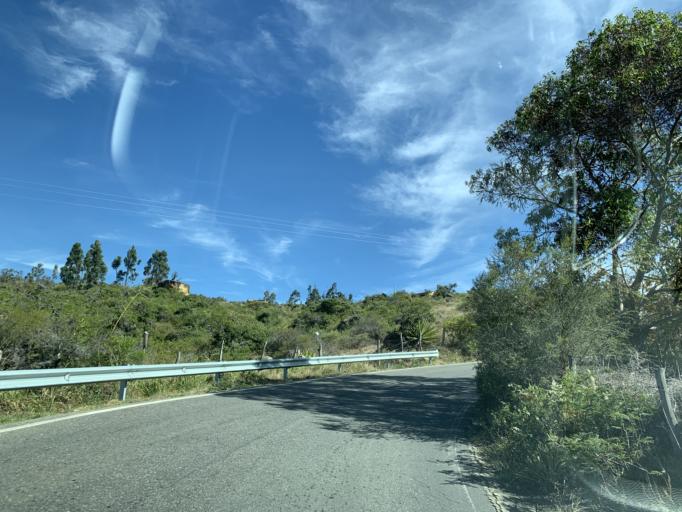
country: CO
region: Boyaca
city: Santa Sofia
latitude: 5.6869
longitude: -73.5886
